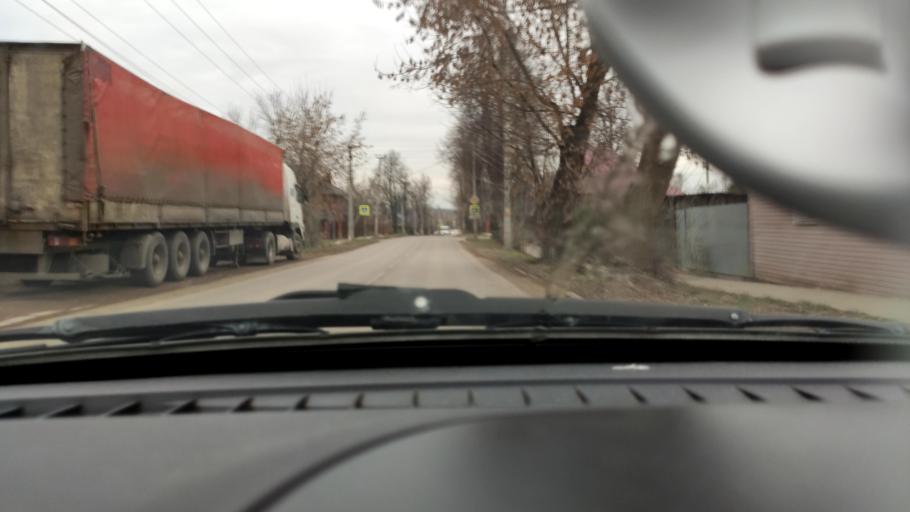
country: RU
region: Perm
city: Perm
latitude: 58.0252
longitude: 56.3339
